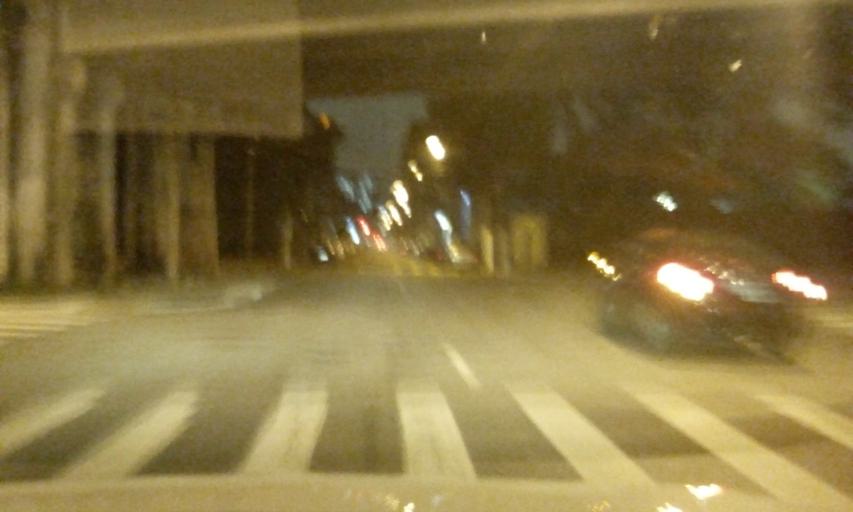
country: BR
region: Sao Paulo
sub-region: Sao Paulo
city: Sao Paulo
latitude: -23.5491
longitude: -46.6210
